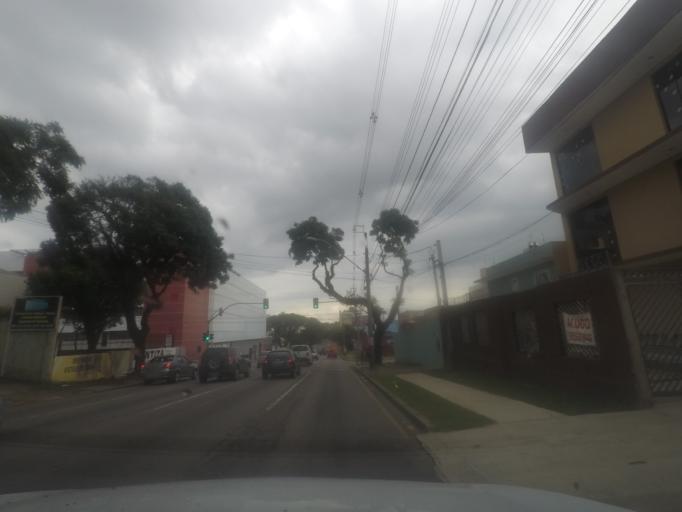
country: BR
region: Parana
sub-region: Sao Jose Dos Pinhais
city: Sao Jose dos Pinhais
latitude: -25.5148
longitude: -49.2973
